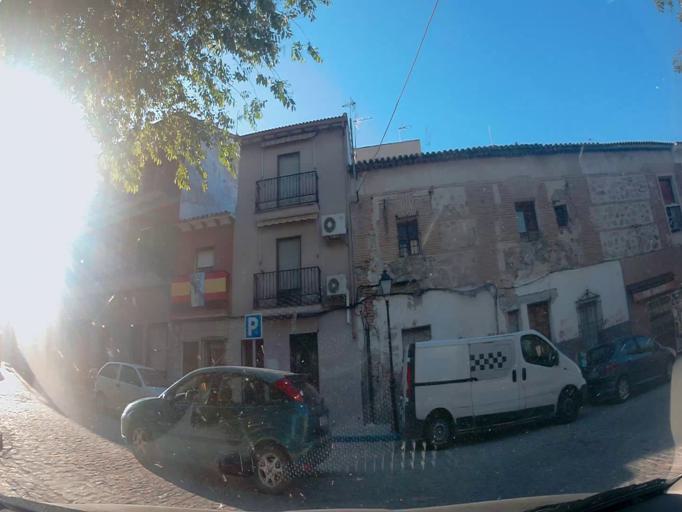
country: ES
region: Castille-La Mancha
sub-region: Province of Toledo
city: Almorox
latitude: 40.2333
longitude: -4.3910
